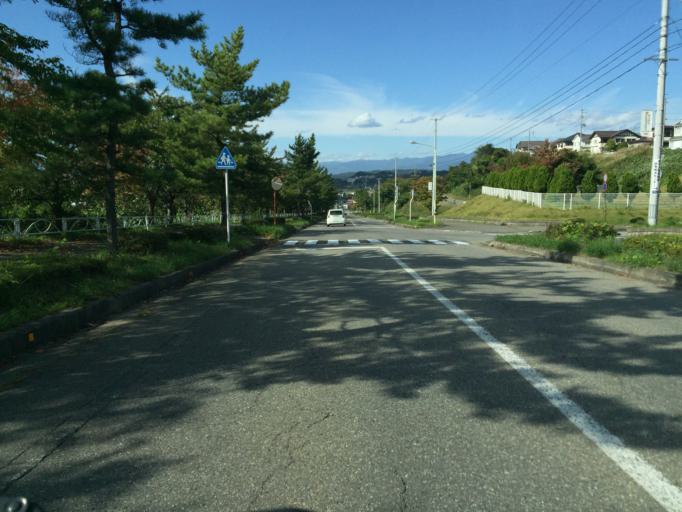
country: JP
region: Fukushima
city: Kitakata
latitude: 37.5297
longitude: 139.9539
